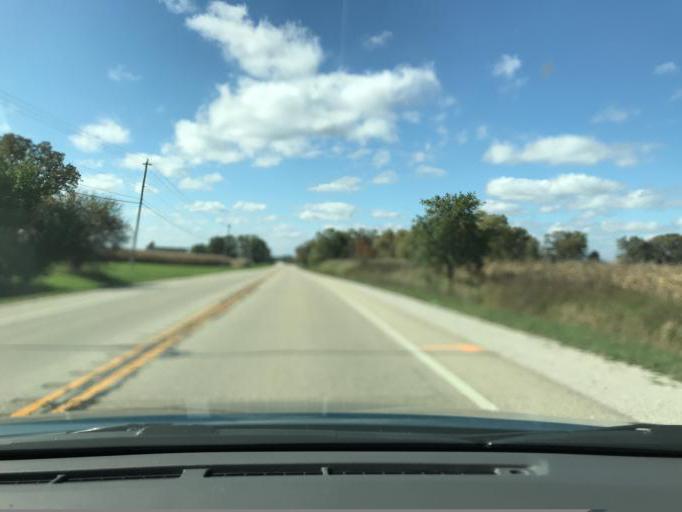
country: US
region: Wisconsin
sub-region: Kenosha County
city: Somers
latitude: 42.6240
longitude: -87.9796
